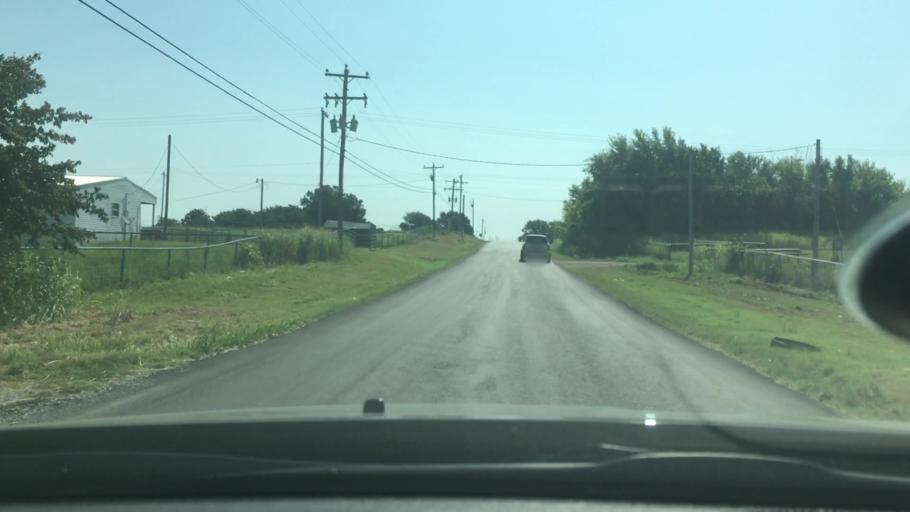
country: US
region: Oklahoma
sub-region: Garvin County
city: Lindsay
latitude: 34.7829
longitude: -97.6001
